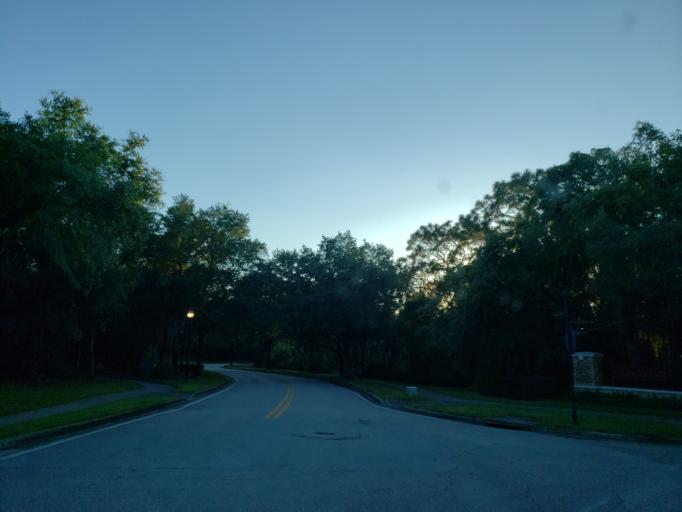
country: US
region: Florida
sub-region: Hillsborough County
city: Boyette
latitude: 27.8379
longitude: -82.2320
